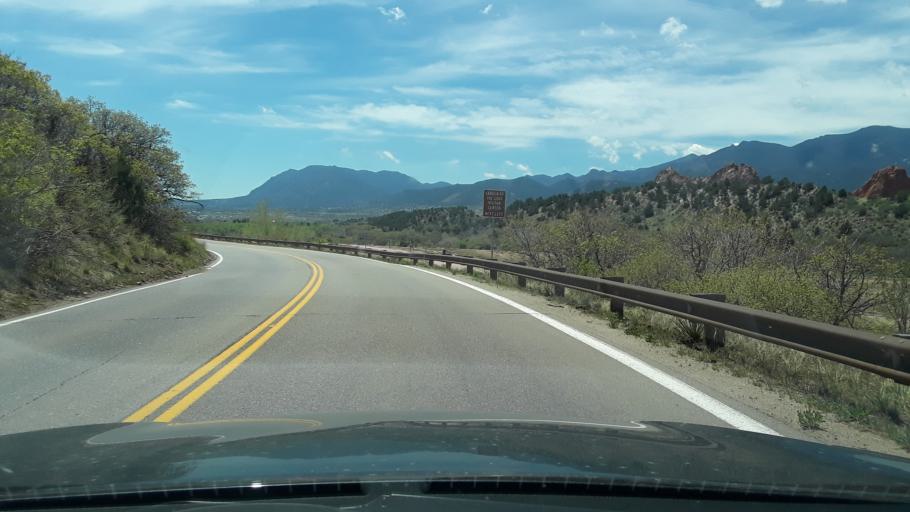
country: US
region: Colorado
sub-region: El Paso County
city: Manitou Springs
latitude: 38.8843
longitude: -104.8740
